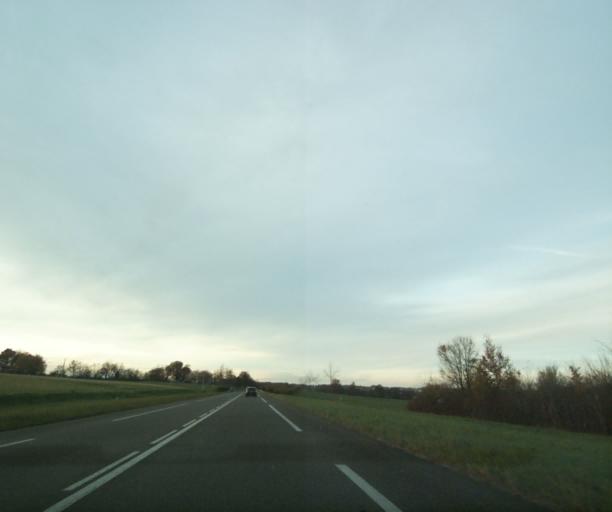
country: FR
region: Aquitaine
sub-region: Departement de la Gironde
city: Bazas
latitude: 44.4212
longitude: -0.2229
